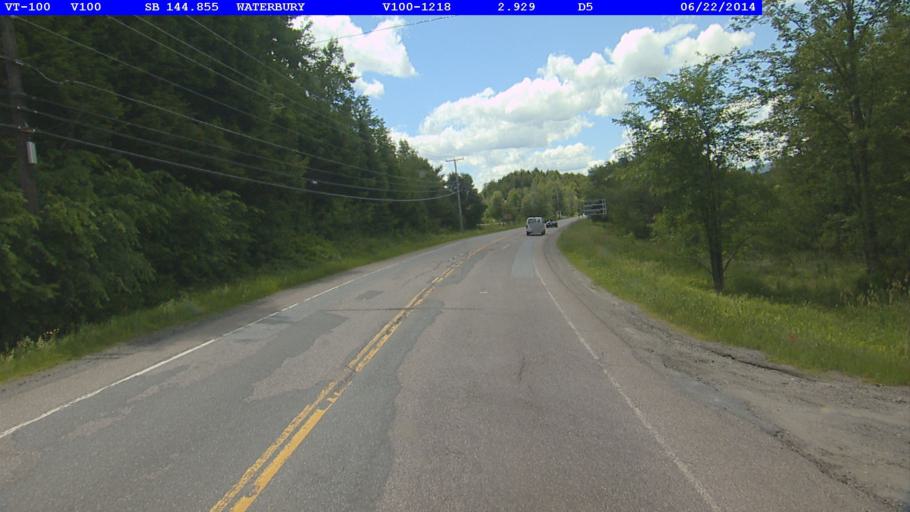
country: US
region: Vermont
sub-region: Washington County
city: Waterbury
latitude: 44.3728
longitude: -72.7264
